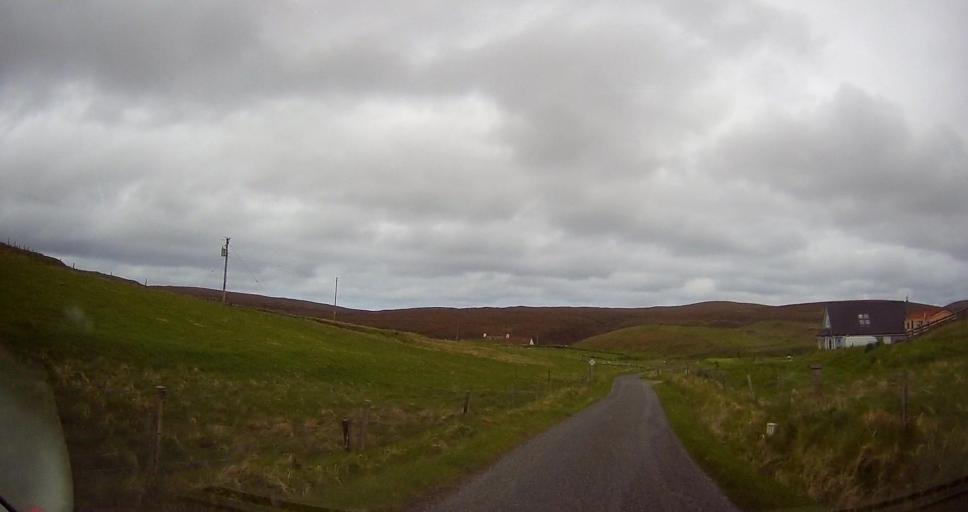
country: GB
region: Scotland
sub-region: Shetland Islands
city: Shetland
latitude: 60.8003
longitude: -0.8741
